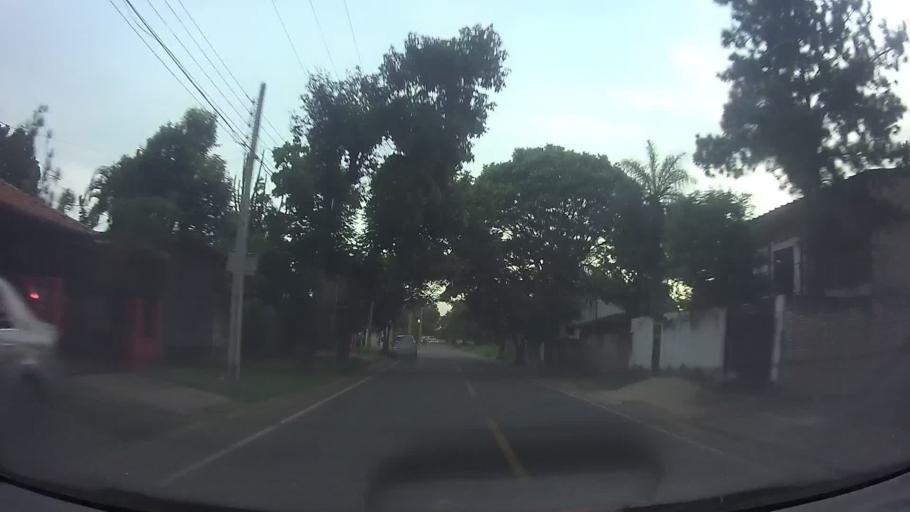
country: PY
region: Central
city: San Lorenzo
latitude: -25.2568
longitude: -57.5031
